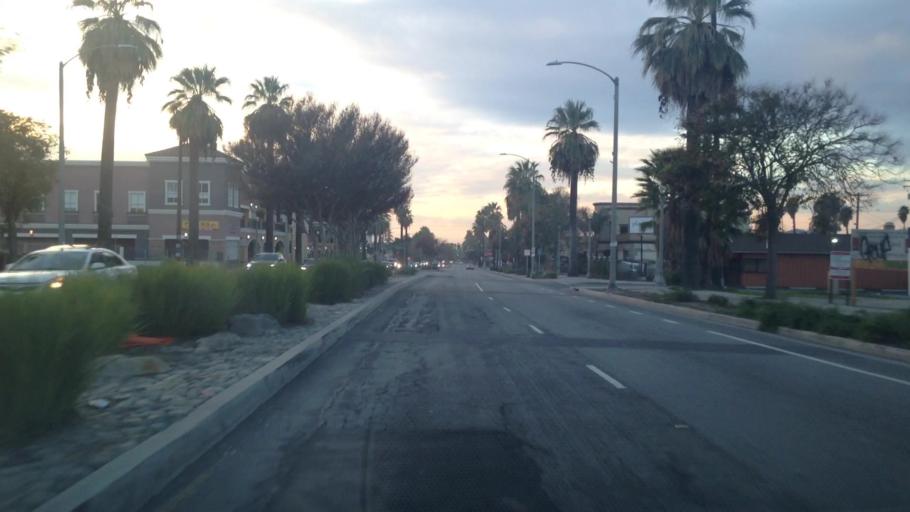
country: US
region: California
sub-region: Riverside County
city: Highgrove
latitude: 33.9757
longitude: -117.3500
